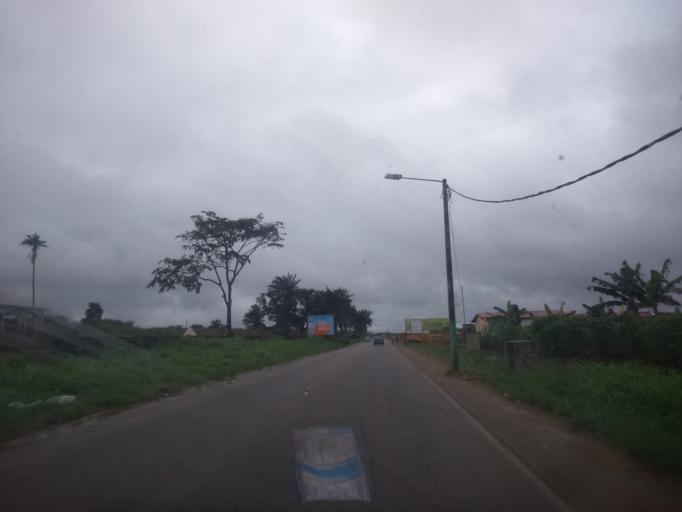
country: CI
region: Sud-Comoe
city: Bonoua
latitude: 5.2750
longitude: -3.5809
